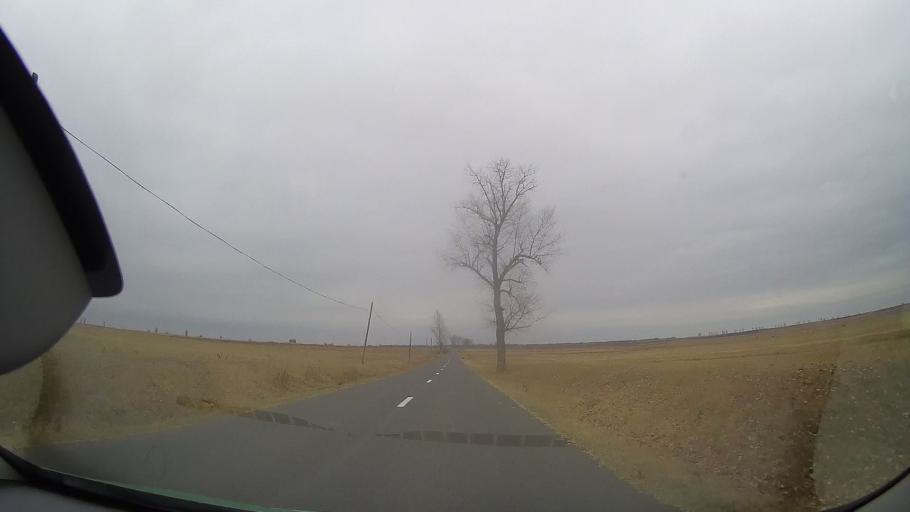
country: RO
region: Braila
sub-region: Comuna Budesti
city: Tataru
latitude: 44.8297
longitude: 27.4080
